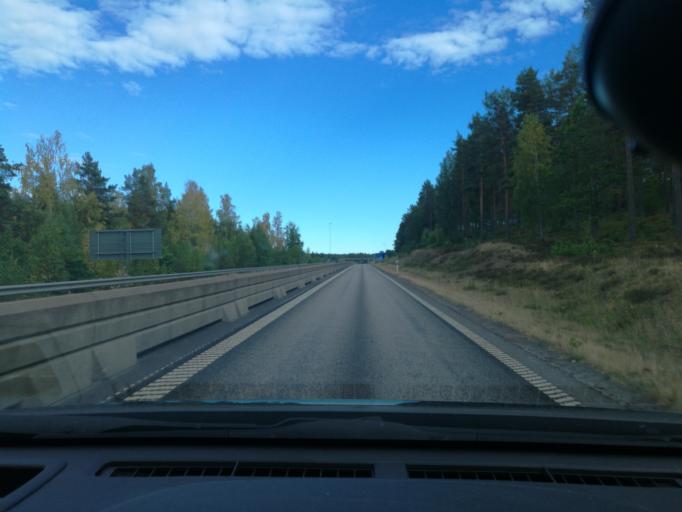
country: SE
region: Kalmar
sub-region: Oskarshamns Kommun
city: Oskarshamn
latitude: 57.3780
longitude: 16.4848
